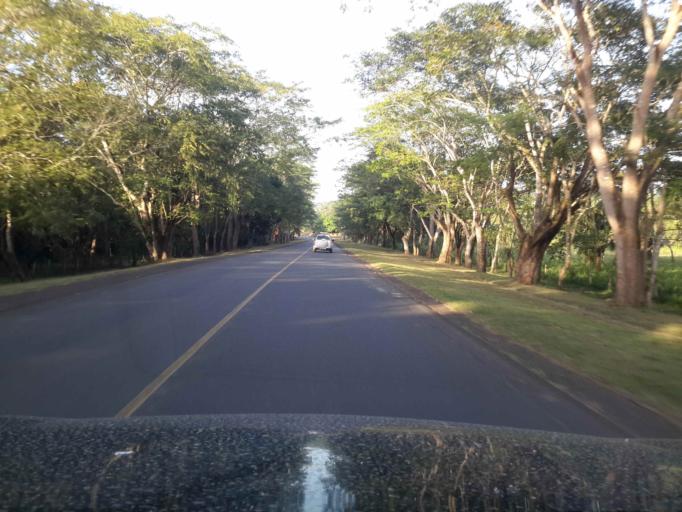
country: NI
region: Rio San Juan
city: San Miguelito
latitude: 11.4619
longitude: -84.8492
